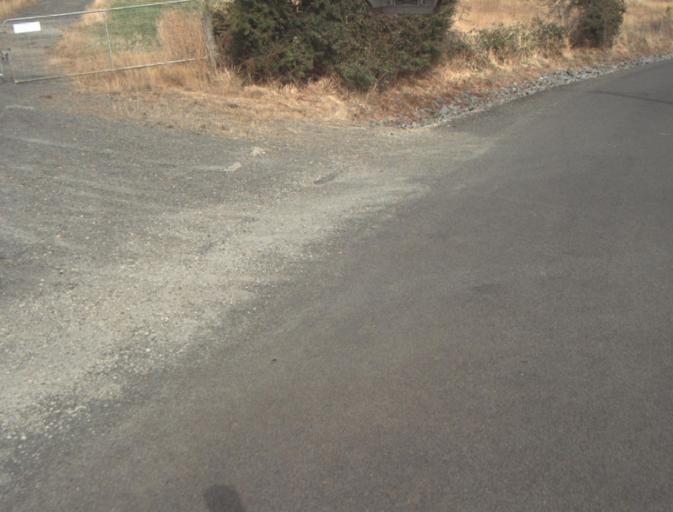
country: AU
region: Tasmania
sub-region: Launceston
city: Mayfield
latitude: -41.3129
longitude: 146.9968
